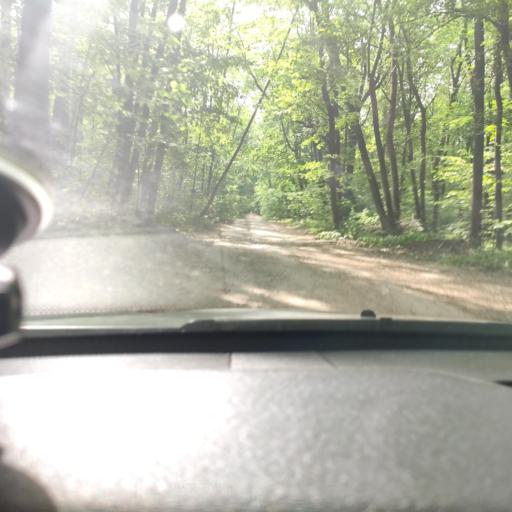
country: RU
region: Samara
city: Novosemeykino
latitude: 53.3273
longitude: 50.2273
